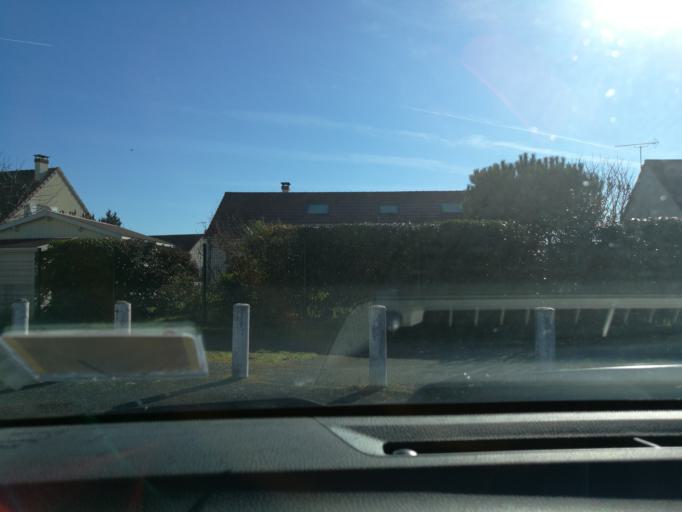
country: FR
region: Centre
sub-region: Departement du Loiret
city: Saint-Ay
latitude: 47.8634
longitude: 1.7607
